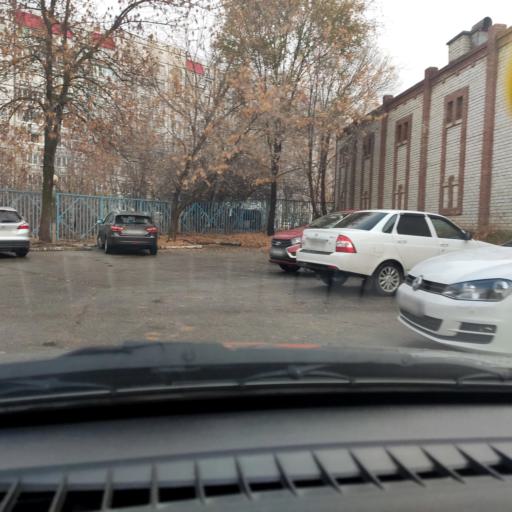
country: RU
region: Samara
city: Tol'yatti
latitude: 53.5228
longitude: 49.3330
